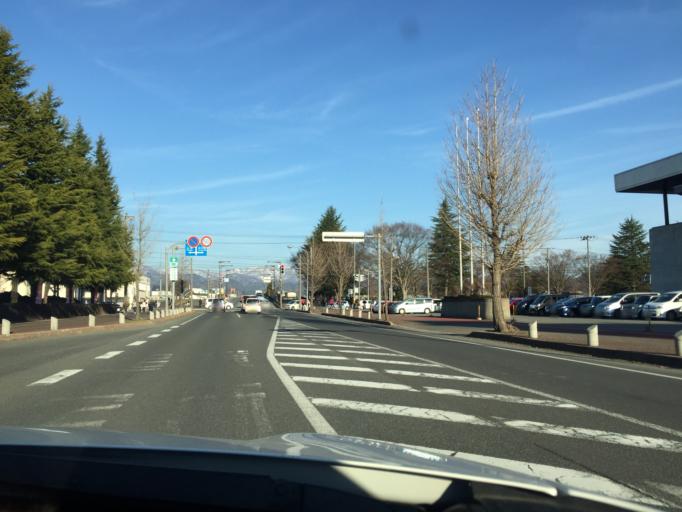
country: JP
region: Yamagata
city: Yonezawa
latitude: 37.9215
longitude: 140.1164
